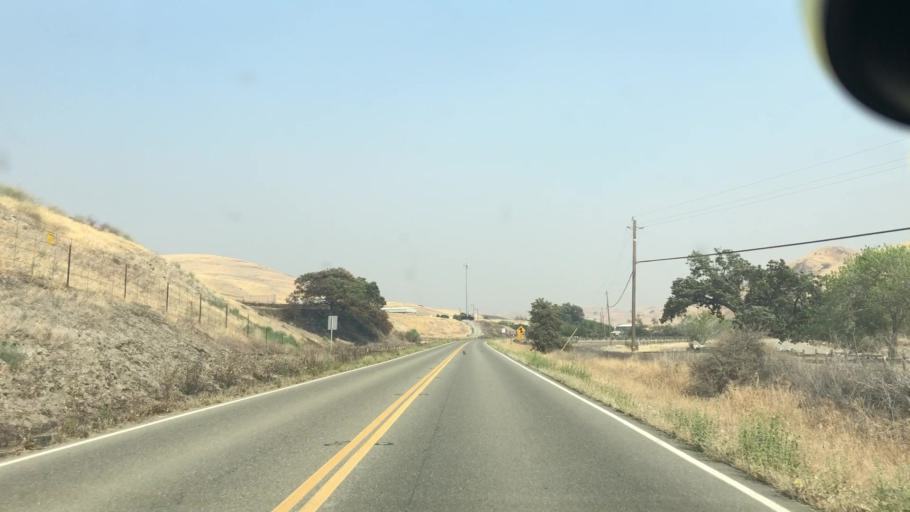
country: US
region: California
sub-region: San Joaquin County
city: Mountain House
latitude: 37.6349
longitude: -121.5474
